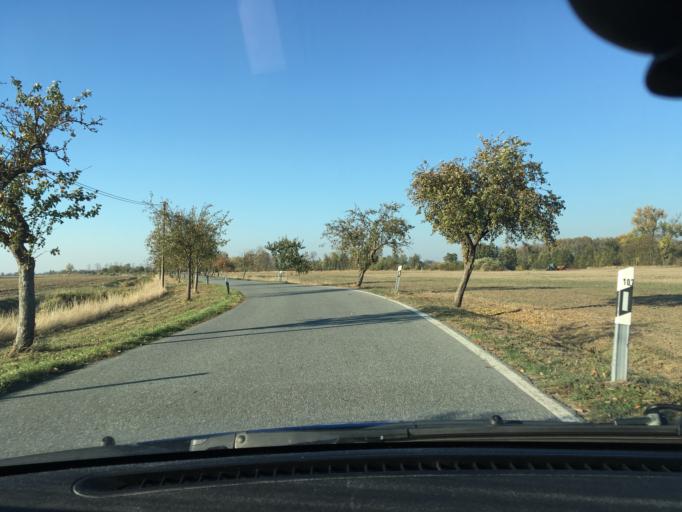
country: DE
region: Lower Saxony
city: Hitzacker
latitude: 53.1793
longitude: 11.0378
